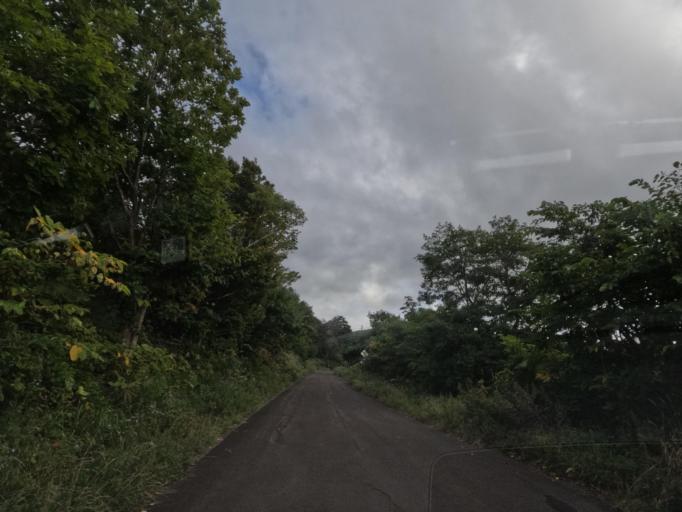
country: JP
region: Hokkaido
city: Muroran
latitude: 42.3309
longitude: 141.0024
